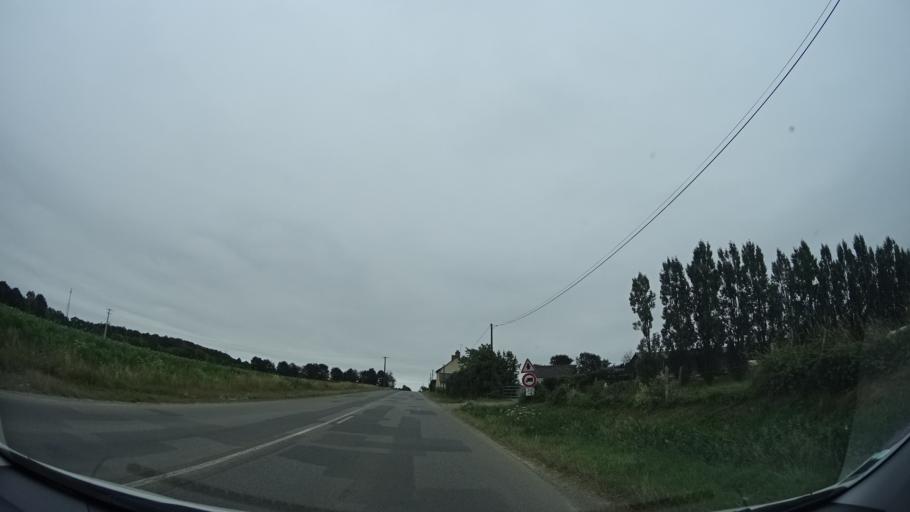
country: FR
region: Brittany
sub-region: Departement d'Ille-et-Vilaine
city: La Meziere
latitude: 48.2299
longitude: -1.7565
